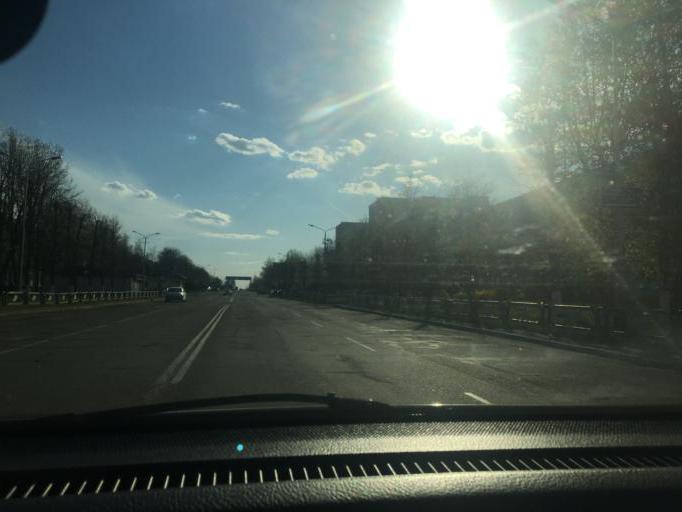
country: BY
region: Mogilev
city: Babruysk
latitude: 53.1703
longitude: 29.1999
